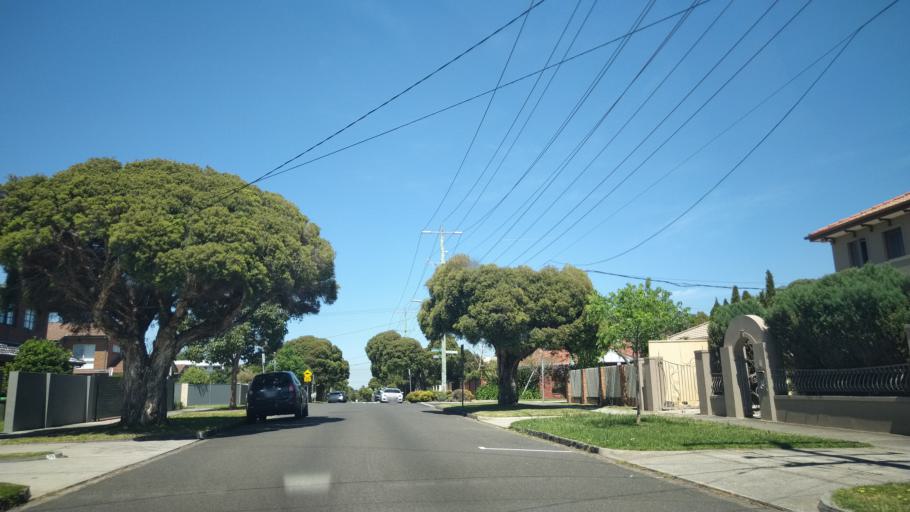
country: AU
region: Victoria
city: Ormond
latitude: -37.8948
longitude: 145.0320
